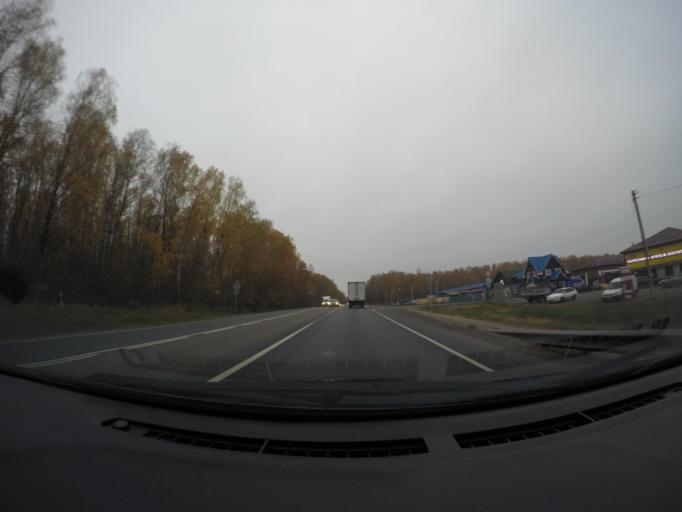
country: RU
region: Moskovskaya
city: Bronnitsy
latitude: 55.3734
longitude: 38.1369
